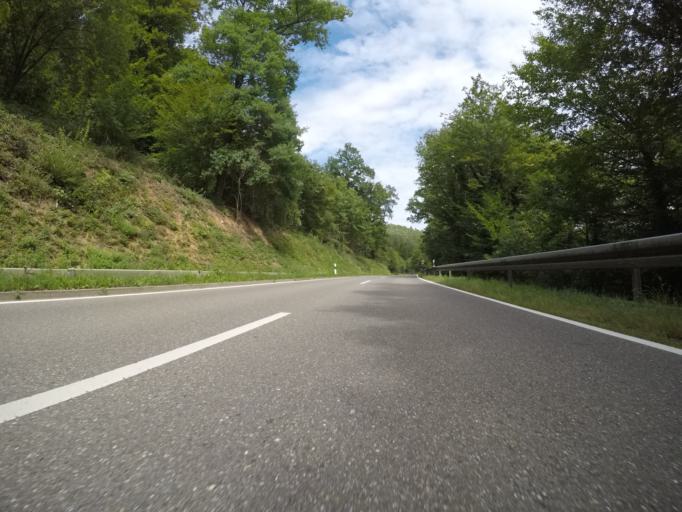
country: DE
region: Baden-Wuerttemberg
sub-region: Tuebingen Region
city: Hirrlingen
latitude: 48.4480
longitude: 8.8253
